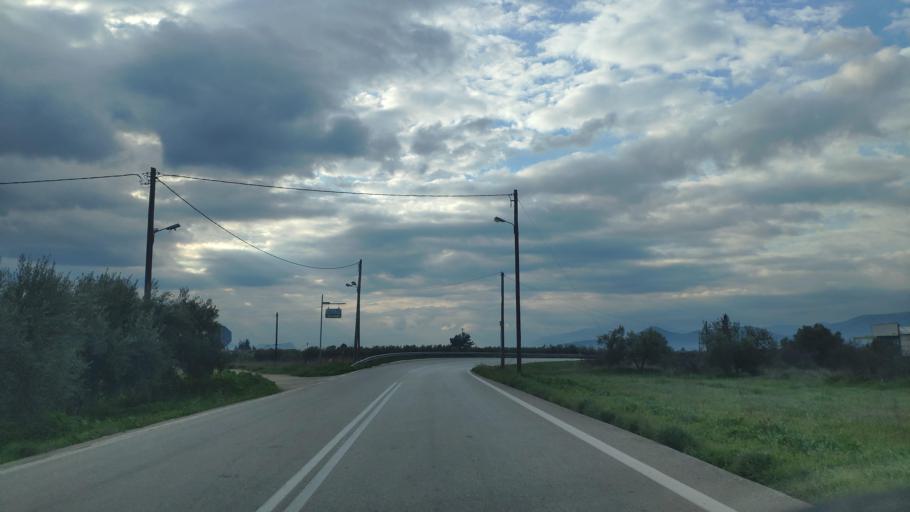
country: GR
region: Peloponnese
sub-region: Nomos Argolidos
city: Koutsopodi
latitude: 37.7119
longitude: 22.7260
